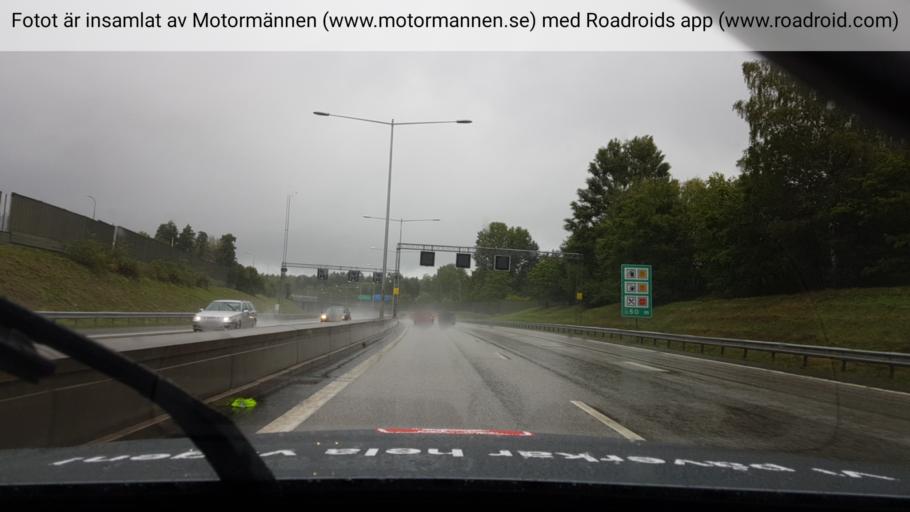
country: SE
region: Stockholm
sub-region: Sodertalje Kommun
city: Soedertaelje
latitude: 59.1907
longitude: 17.6514
